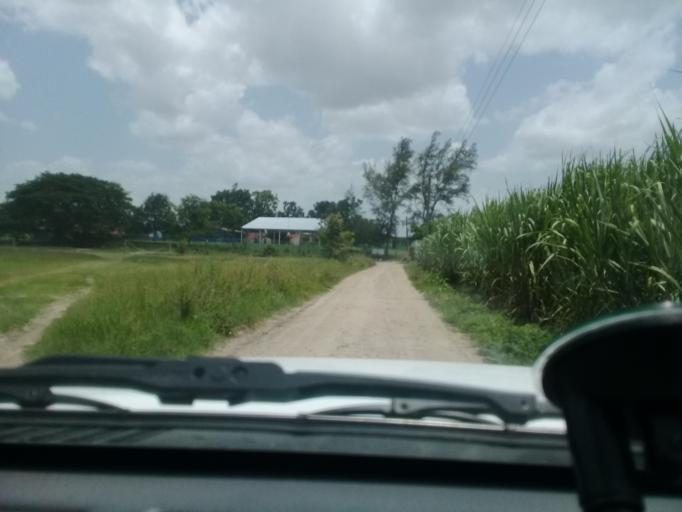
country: MX
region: Veracruz
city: Panuco
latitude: 22.1268
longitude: -98.0553
